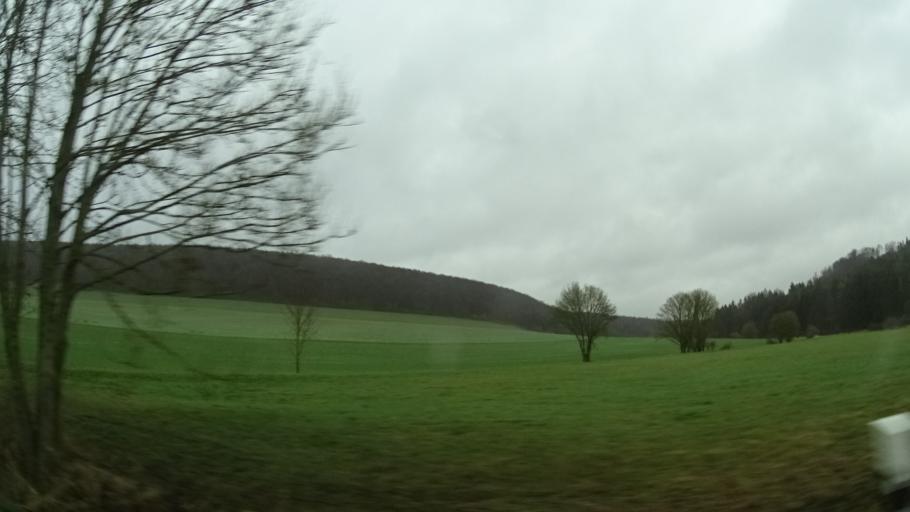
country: DE
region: Thuringia
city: Juchsen
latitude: 50.4672
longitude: 10.5343
